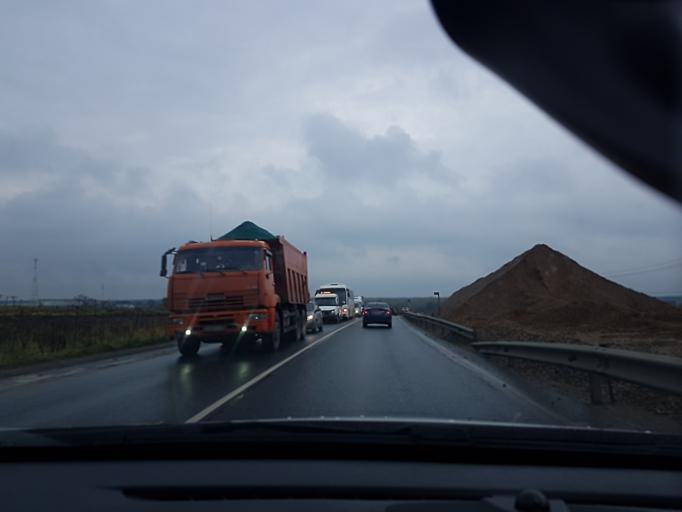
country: RU
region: Moskovskaya
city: Istra
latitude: 55.9215
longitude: 36.9461
